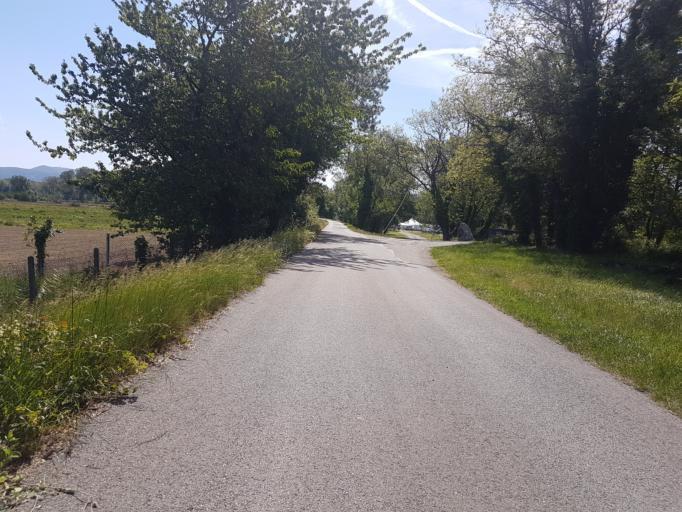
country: FR
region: Rhone-Alpes
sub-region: Departement de l'Ardeche
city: Le Pouzin
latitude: 44.7314
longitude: 4.7478
